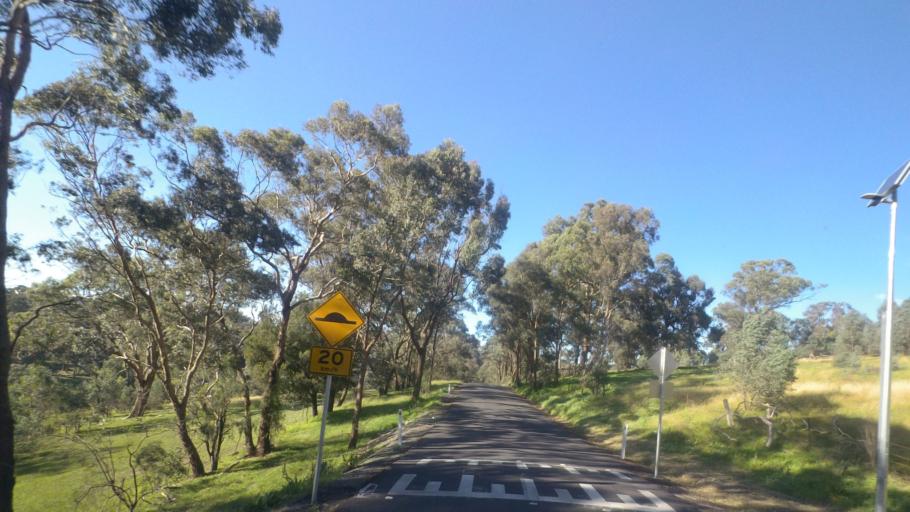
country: AU
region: Victoria
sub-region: Nillumbik
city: Research
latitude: -37.6902
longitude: 145.1694
